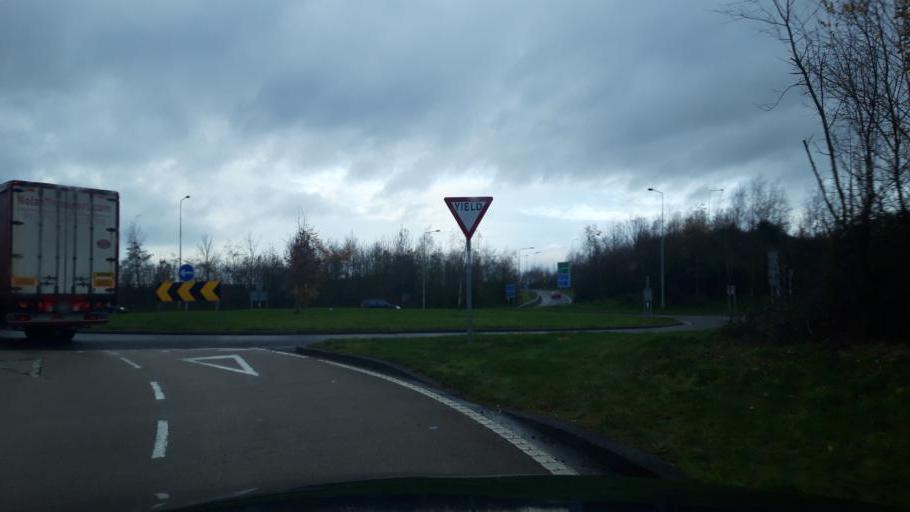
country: IE
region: Leinster
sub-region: County Carlow
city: Carlow
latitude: 52.8013
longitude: -6.8800
